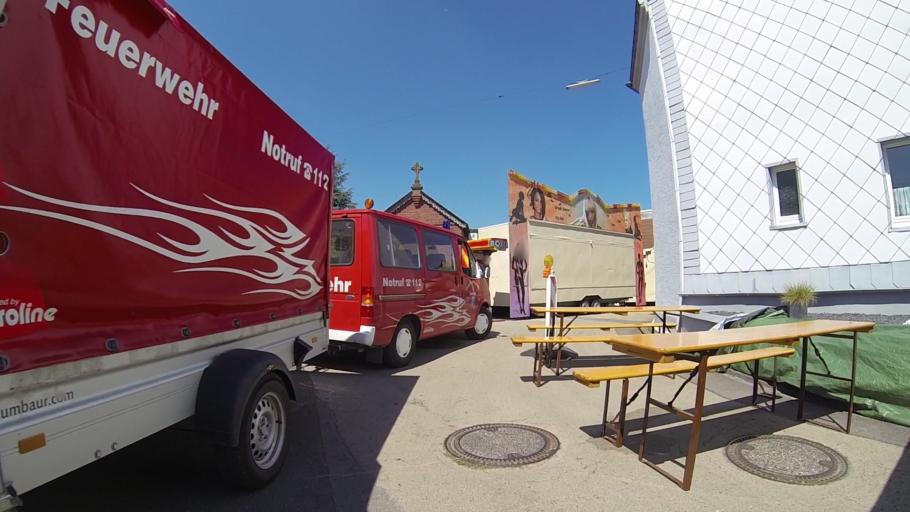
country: DE
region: Rheinland-Pfalz
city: Temmels
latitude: 49.6904
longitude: 6.4608
